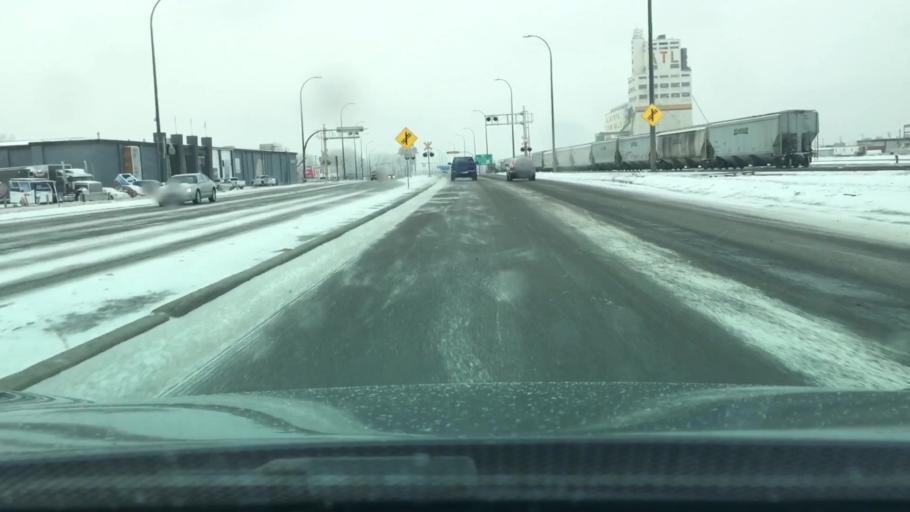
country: CA
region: Alberta
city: Lethbridge
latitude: 49.6983
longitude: -112.7968
